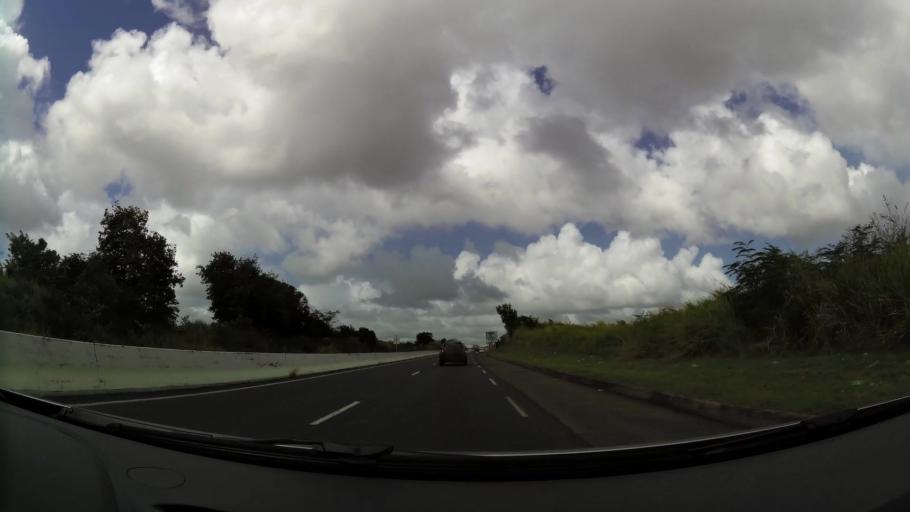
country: MQ
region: Martinique
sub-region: Martinique
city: Fort-de-France
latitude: 14.6090
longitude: -61.0423
